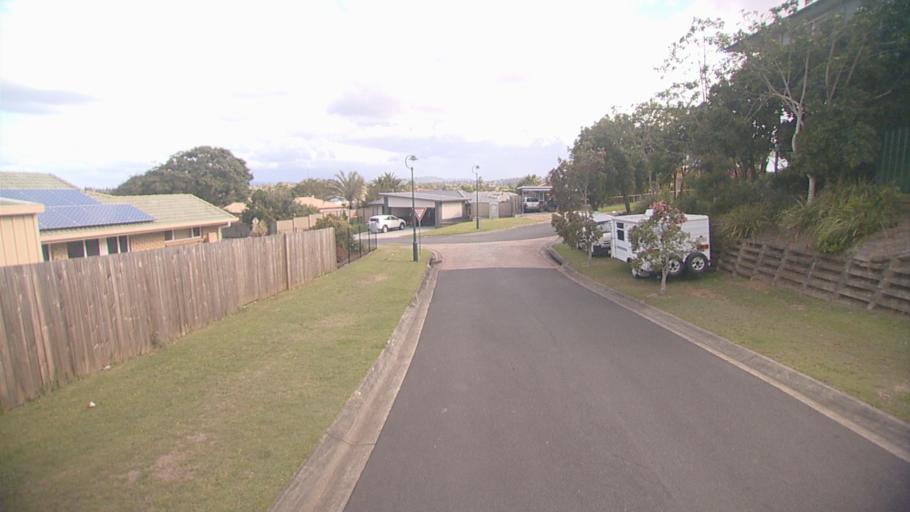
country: AU
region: Queensland
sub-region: Logan
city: Slacks Creek
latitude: -27.6777
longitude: 153.1736
